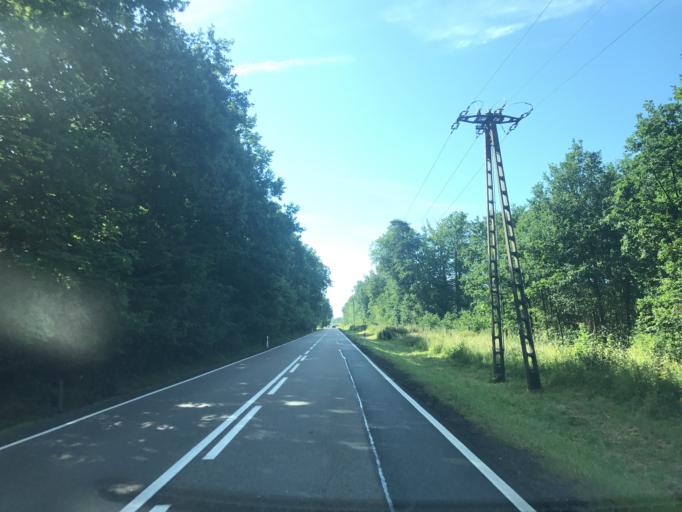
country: PL
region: Pomeranian Voivodeship
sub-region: Powiat czluchowski
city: Czluchow
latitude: 53.6972
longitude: 17.2934
